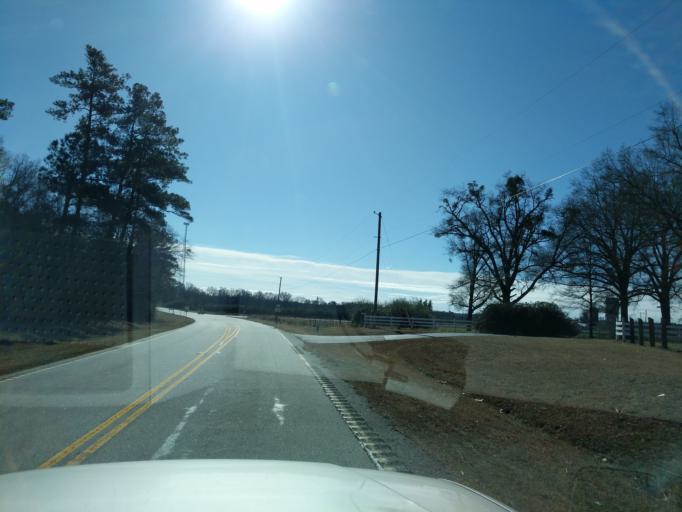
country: US
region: South Carolina
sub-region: Saluda County
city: Saluda
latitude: 34.0499
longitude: -81.8184
